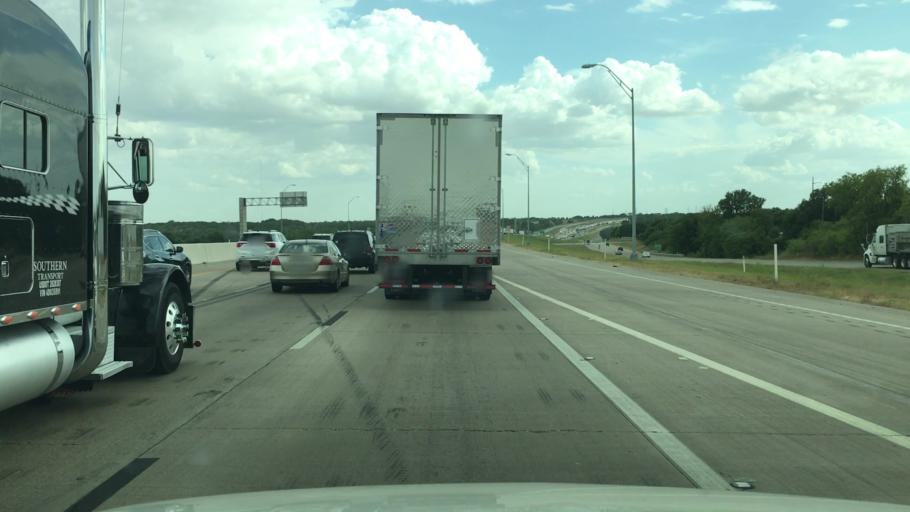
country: US
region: Texas
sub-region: McLennan County
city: Lorena
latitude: 31.3426
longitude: -97.2217
